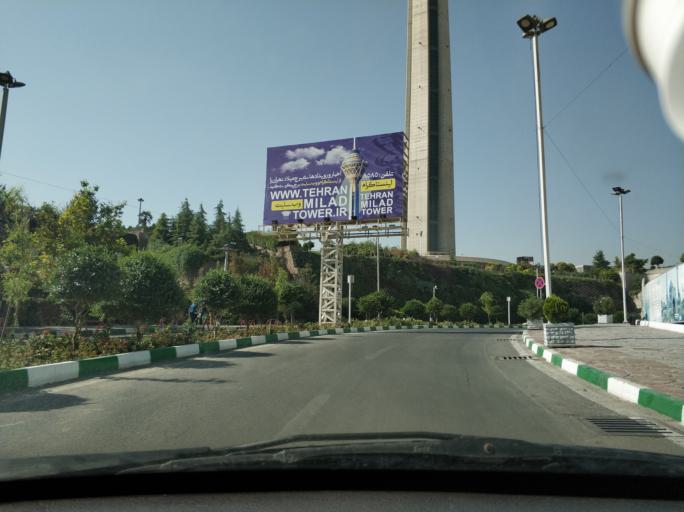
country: IR
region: Tehran
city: Tehran
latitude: 35.7463
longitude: 51.3778
